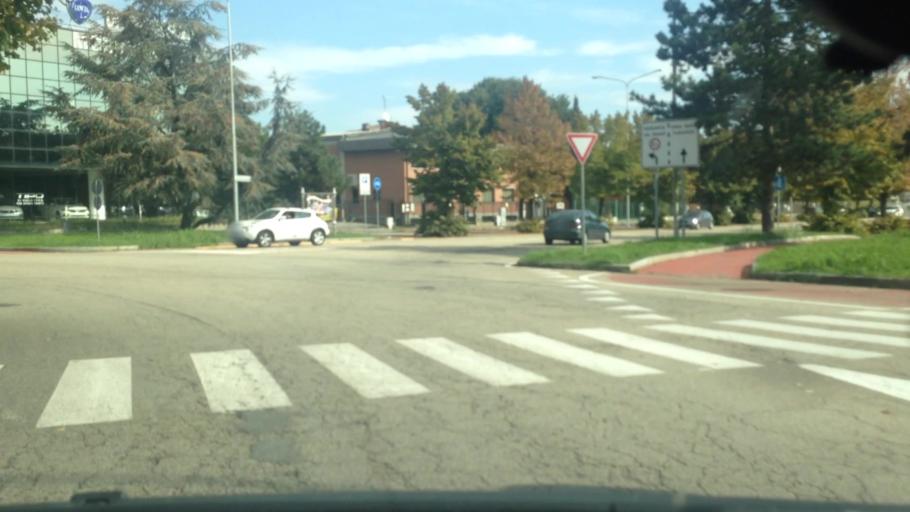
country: IT
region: Piedmont
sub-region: Provincia di Torino
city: Venaria Reale
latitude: 45.1169
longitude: 7.6442
